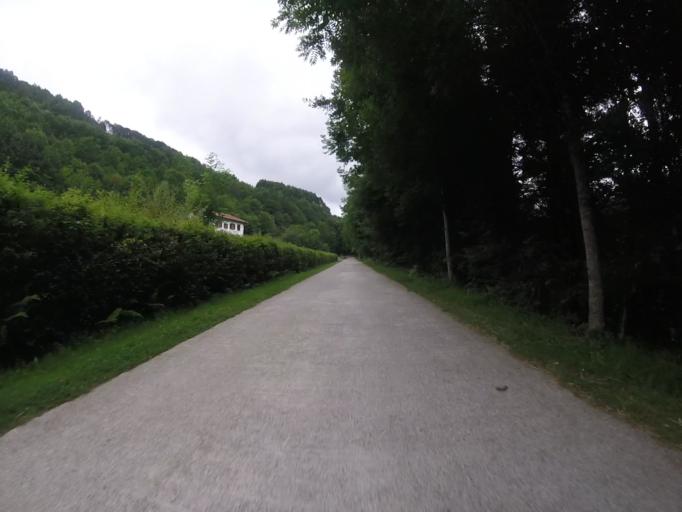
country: ES
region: Navarre
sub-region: Provincia de Navarra
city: Sunbilla
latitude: 43.1543
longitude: -1.6704
